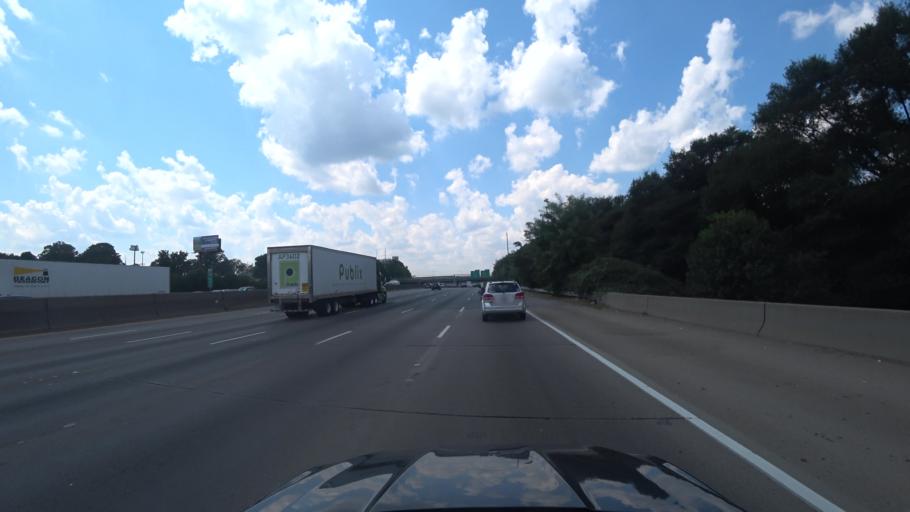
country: US
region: Georgia
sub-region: DeKalb County
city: Doraville
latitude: 33.9030
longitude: -84.2738
